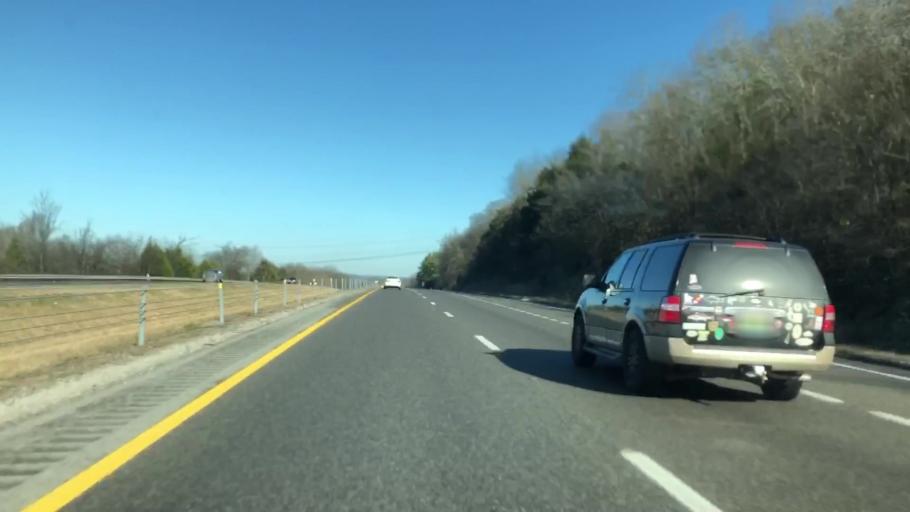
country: US
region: Alabama
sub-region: Limestone County
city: Ardmore
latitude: 35.0190
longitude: -86.8791
